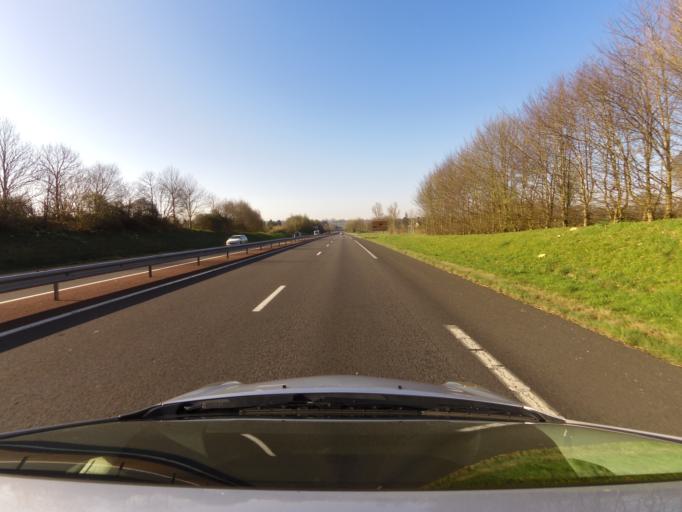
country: FR
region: Lower Normandy
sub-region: Departement de la Manche
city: Villedieu-les-Poeles
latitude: 48.8114
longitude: -1.2560
